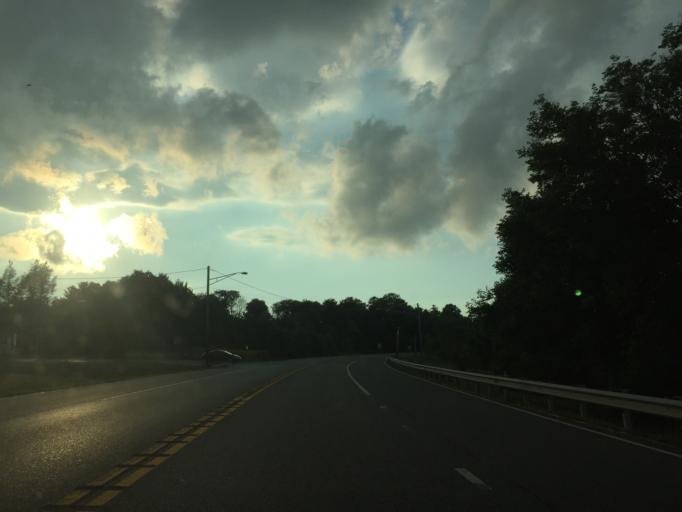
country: US
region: Maryland
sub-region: Harford County
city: Jarrettsville
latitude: 39.5569
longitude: -76.4952
